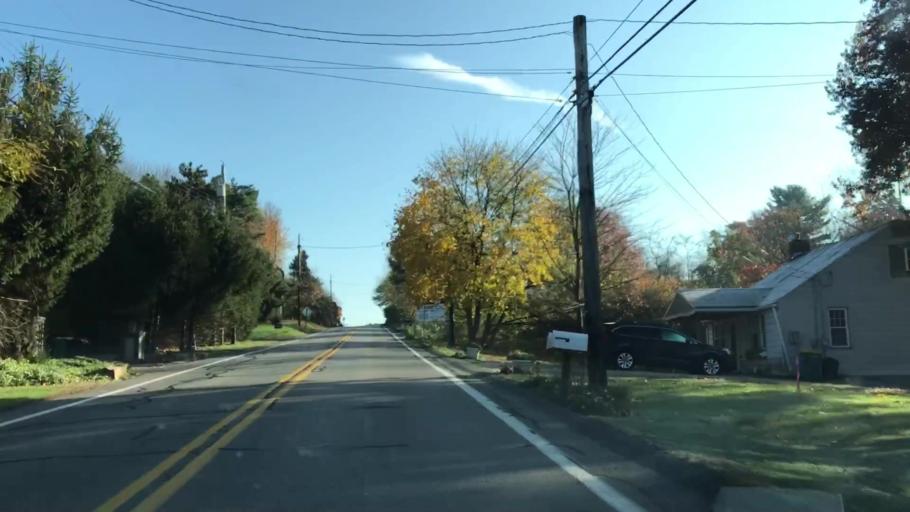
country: US
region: Pennsylvania
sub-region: Allegheny County
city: Franklin Park
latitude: 40.6092
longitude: -80.1104
